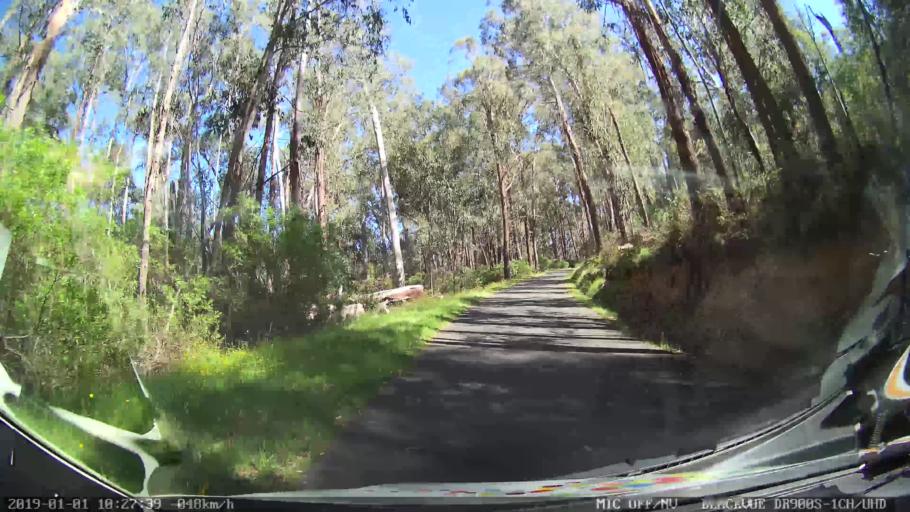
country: AU
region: New South Wales
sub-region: Snowy River
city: Jindabyne
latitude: -36.0648
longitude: 148.2370
